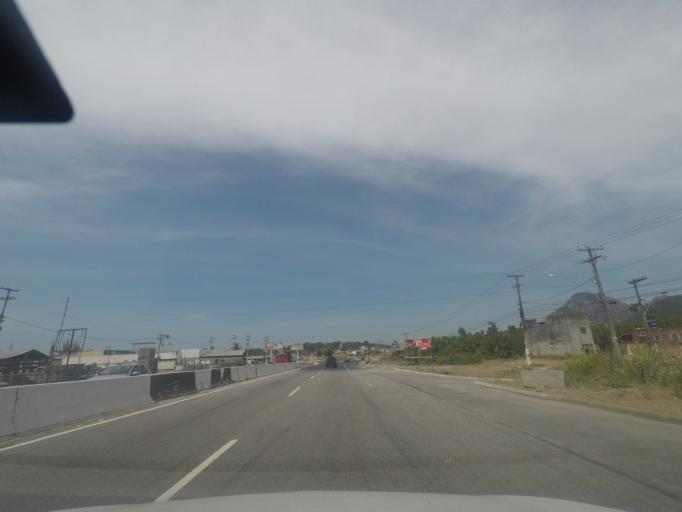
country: BR
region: Rio de Janeiro
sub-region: Marica
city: Marica
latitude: -22.9293
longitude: -42.8710
